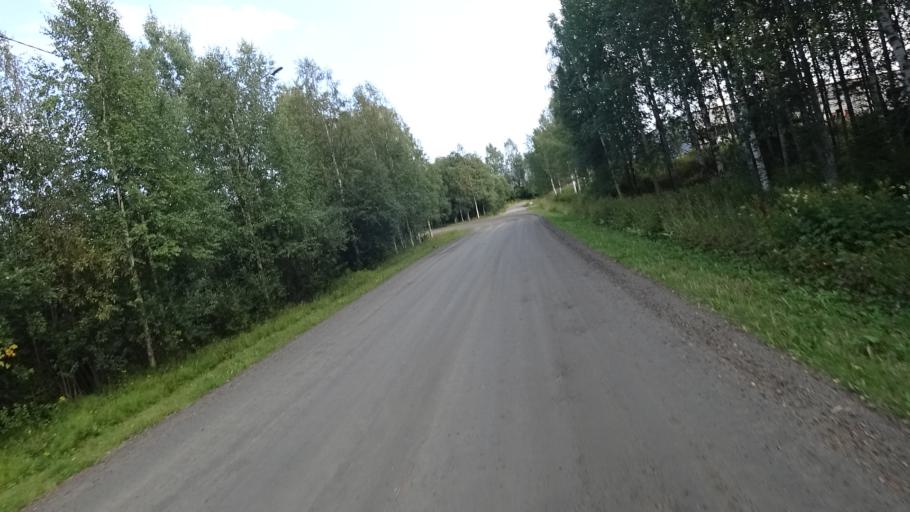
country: FI
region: North Karelia
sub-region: Joensuu
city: Ilomantsi
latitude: 62.6704
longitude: 30.9475
